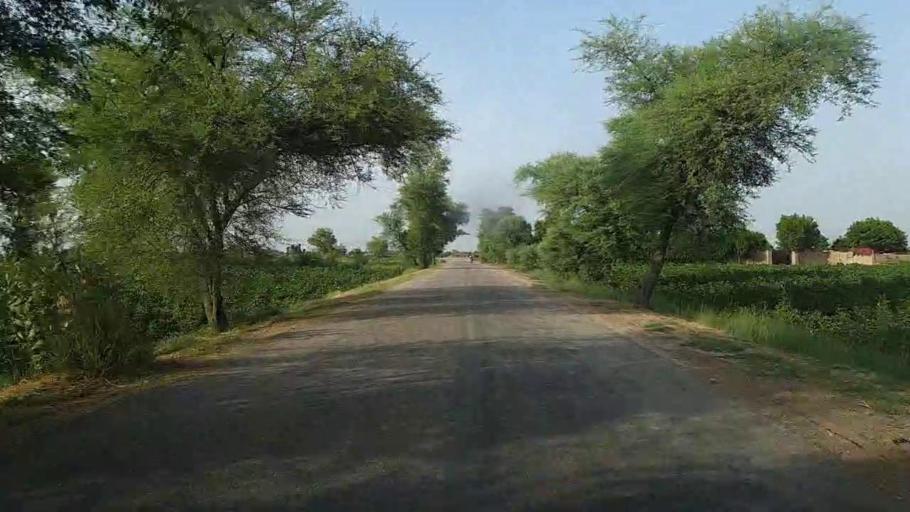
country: PK
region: Sindh
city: Ubauro
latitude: 28.1007
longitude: 69.8112
